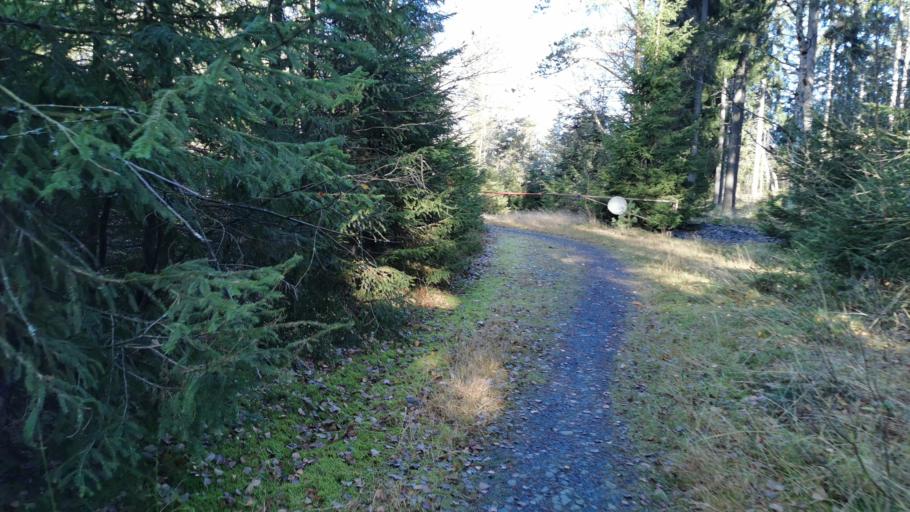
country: DE
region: Bavaria
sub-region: Upper Franconia
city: Reichenbach
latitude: 50.4595
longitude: 11.4395
